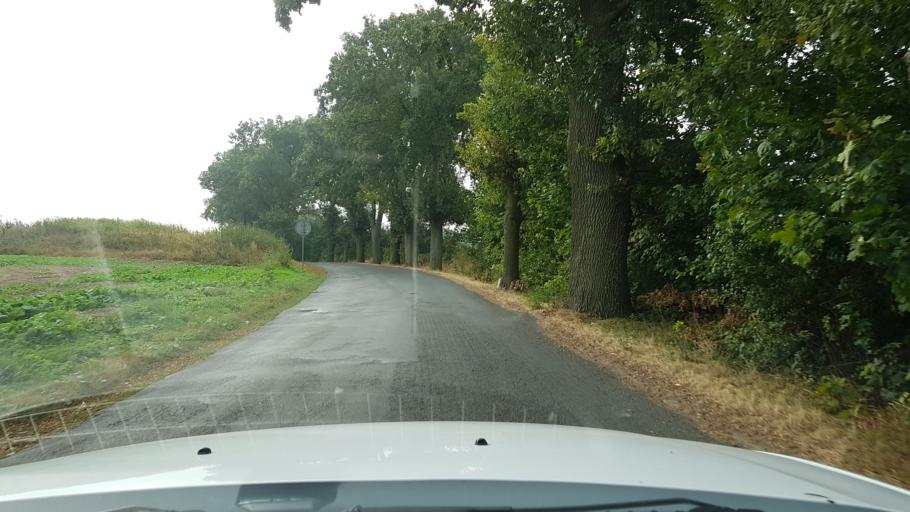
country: PL
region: West Pomeranian Voivodeship
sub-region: Powiat gryfinski
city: Moryn
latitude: 52.8966
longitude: 14.3763
